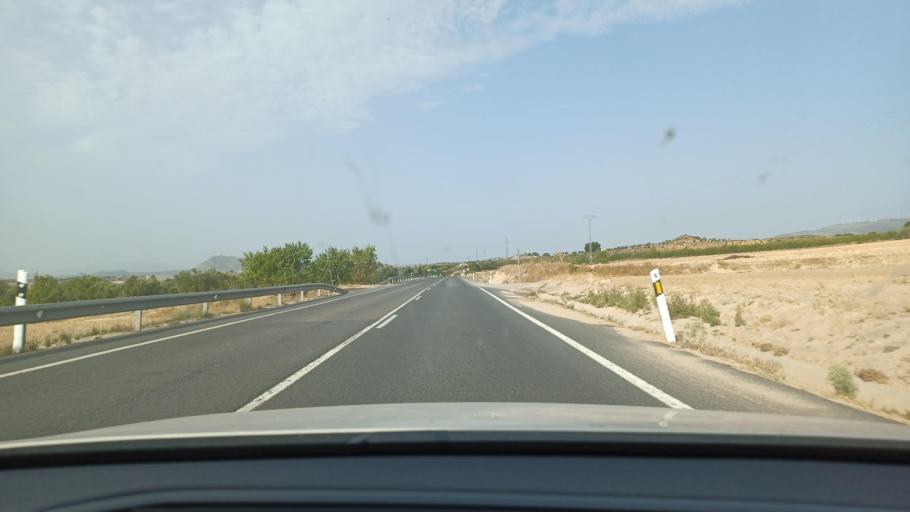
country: ES
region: Valencia
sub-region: Provincia de Valencia
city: La Font de la Figuera
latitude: 38.7440
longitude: -0.9239
